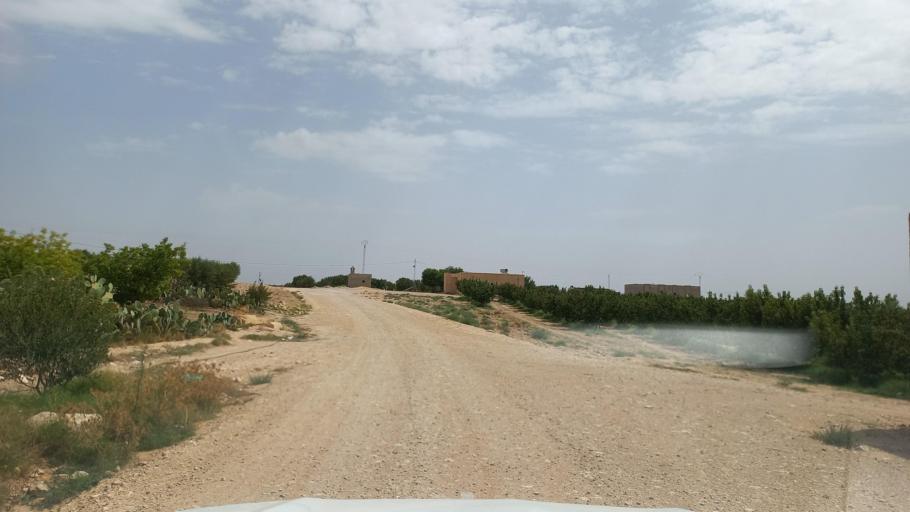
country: TN
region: Al Qasrayn
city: Kasserine
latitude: 35.2823
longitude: 9.0065
